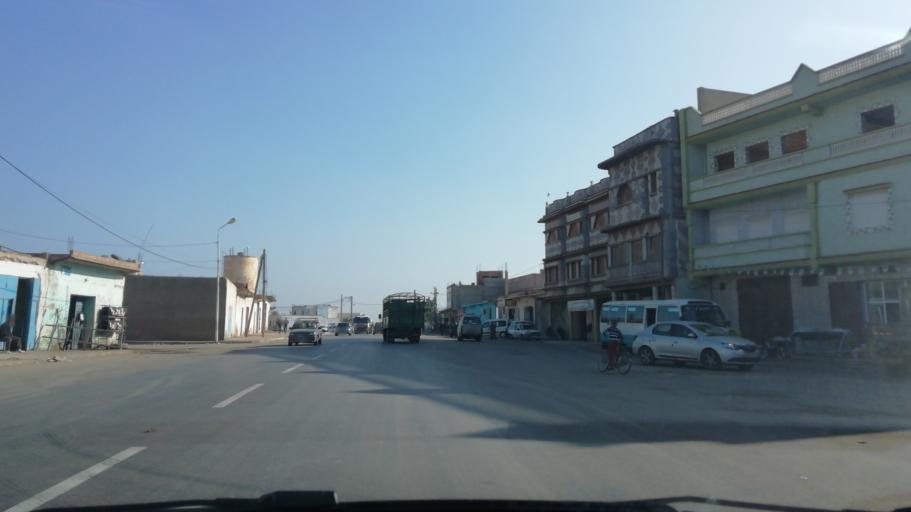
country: DZ
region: Mostaganem
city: Mostaganem
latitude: 35.7398
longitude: -0.0279
